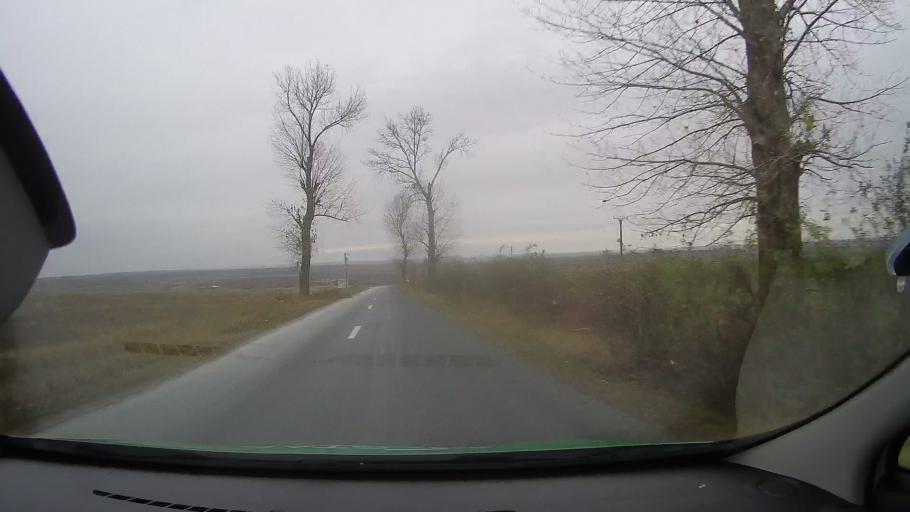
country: RO
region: Constanta
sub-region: Comuna Pantelimon
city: Pantelimon
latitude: 44.5871
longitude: 28.3153
